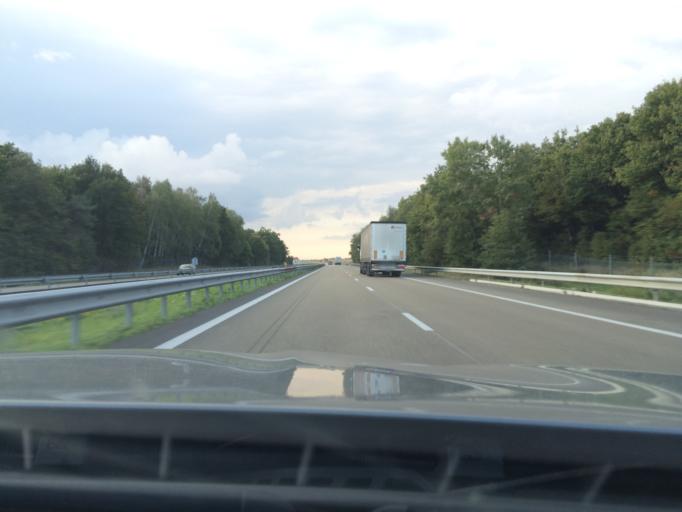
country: FR
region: Ile-de-France
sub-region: Departement de Seine-et-Marne
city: Egreville
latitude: 48.1465
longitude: 2.9056
